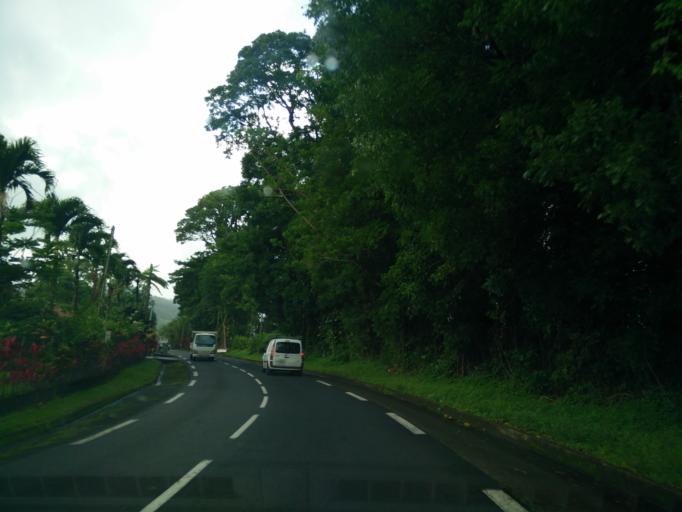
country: MQ
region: Martinique
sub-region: Martinique
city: Le Morne-Rouge
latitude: 14.7636
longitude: -61.1194
